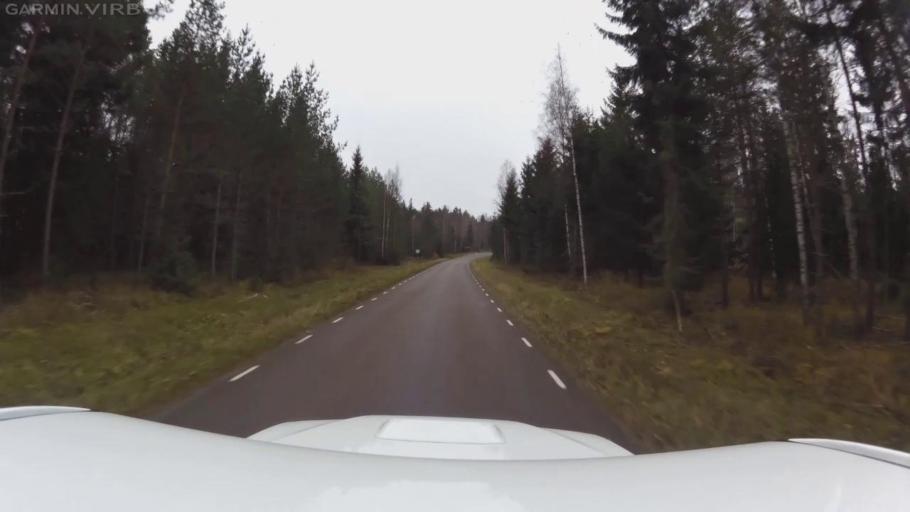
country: SE
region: OEstergoetland
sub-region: Mjolby Kommun
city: Mantorp
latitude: 58.1655
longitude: 15.3967
